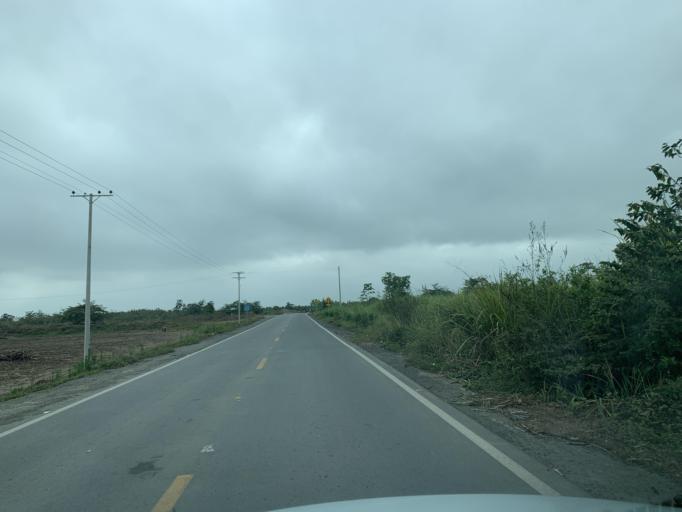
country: EC
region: Guayas
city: Coronel Marcelino Mariduena
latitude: -2.3057
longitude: -79.5033
